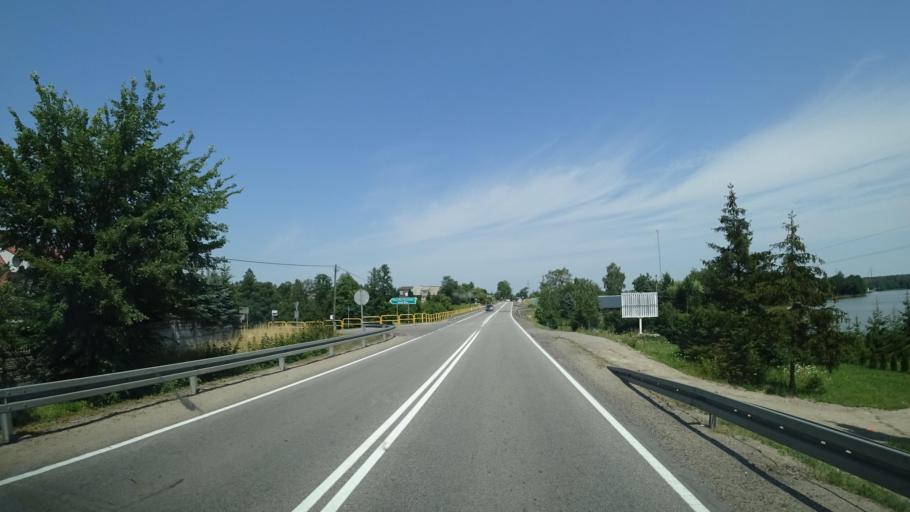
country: PL
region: Pomeranian Voivodeship
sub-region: Powiat koscierski
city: Koscierzyna
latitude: 54.1452
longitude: 18.0248
